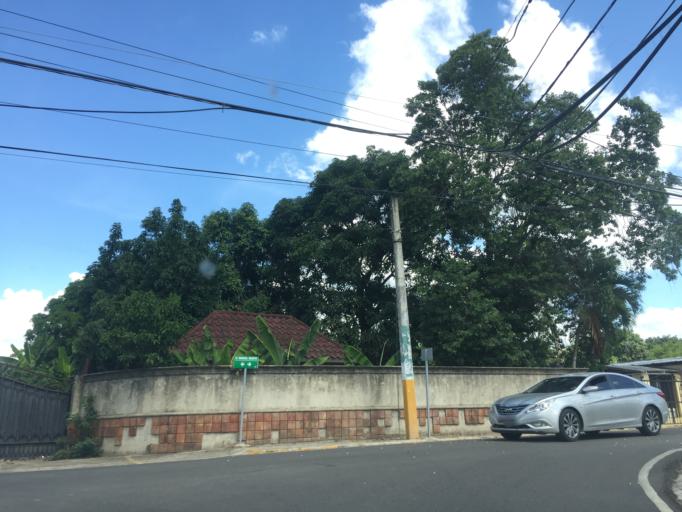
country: DO
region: Santiago
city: Licey al Medio
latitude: 19.3771
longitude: -70.6000
